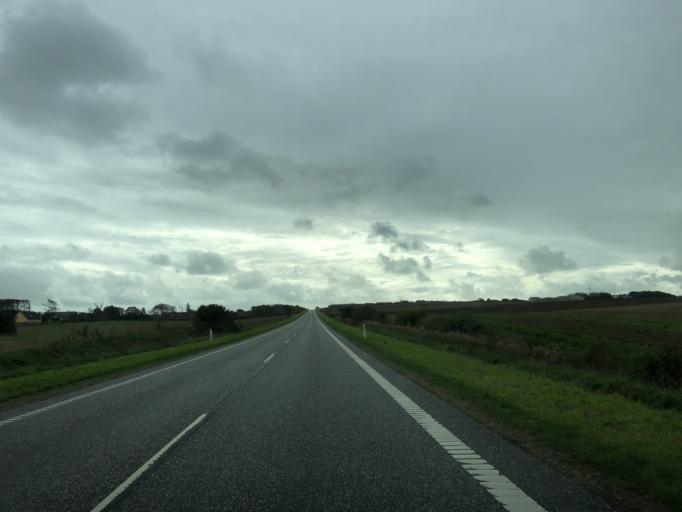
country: DK
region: North Denmark
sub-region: Thisted Kommune
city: Hurup
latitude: 56.7656
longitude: 8.4565
